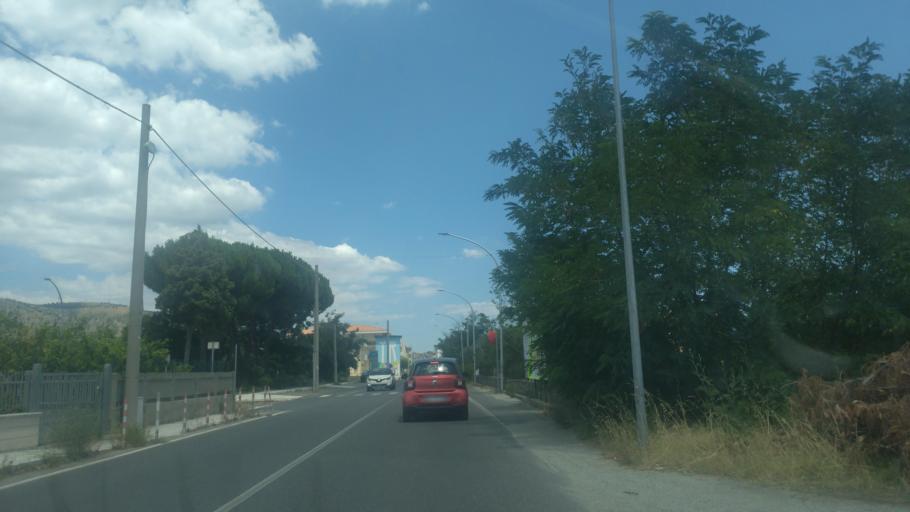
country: IT
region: Calabria
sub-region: Provincia di Catanzaro
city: Montepaone Lido
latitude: 38.7244
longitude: 16.5374
